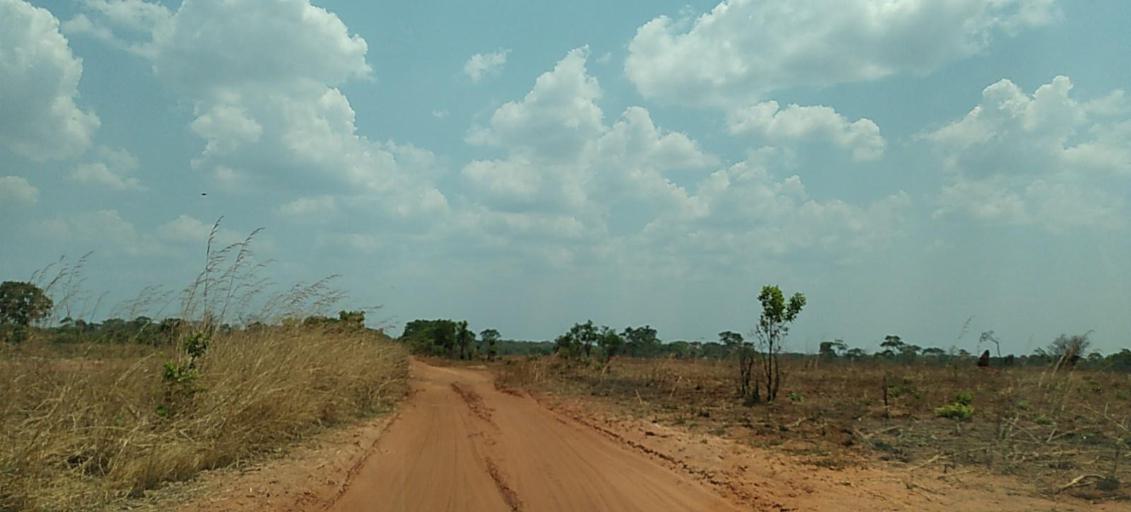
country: ZM
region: Copperbelt
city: Mpongwe
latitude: -13.6626
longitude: 28.0240
